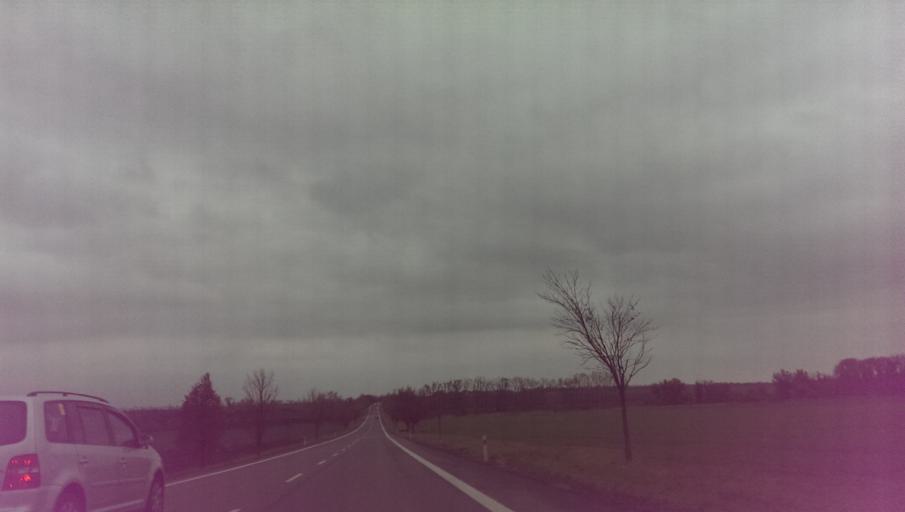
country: CZ
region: South Moravian
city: Olbramovice
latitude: 48.9405
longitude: 16.3746
